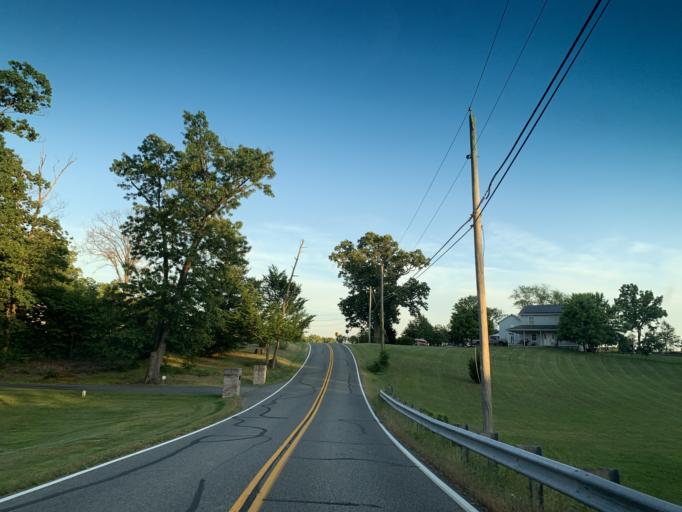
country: US
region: Maryland
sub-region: Cecil County
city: Perryville
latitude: 39.6271
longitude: -76.0617
